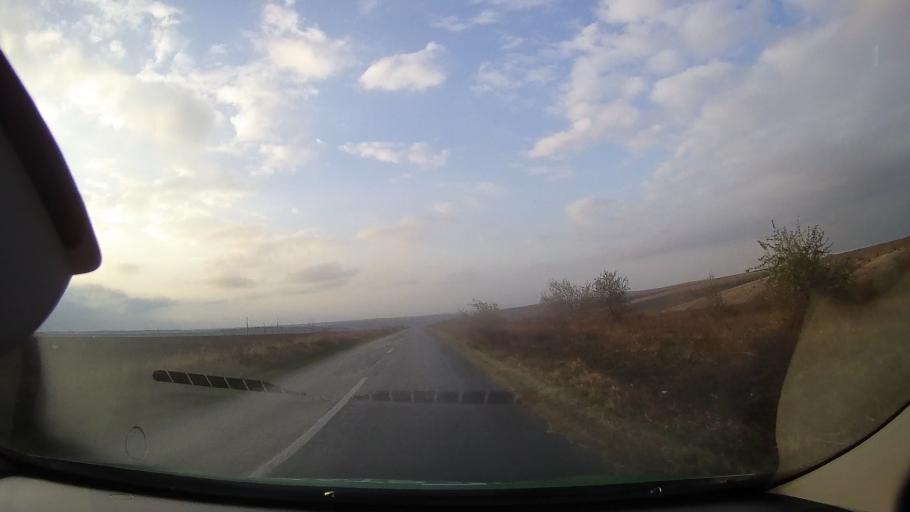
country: RO
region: Constanta
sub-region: Comuna Adamclisi
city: Adamclisi
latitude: 44.0181
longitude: 27.8899
